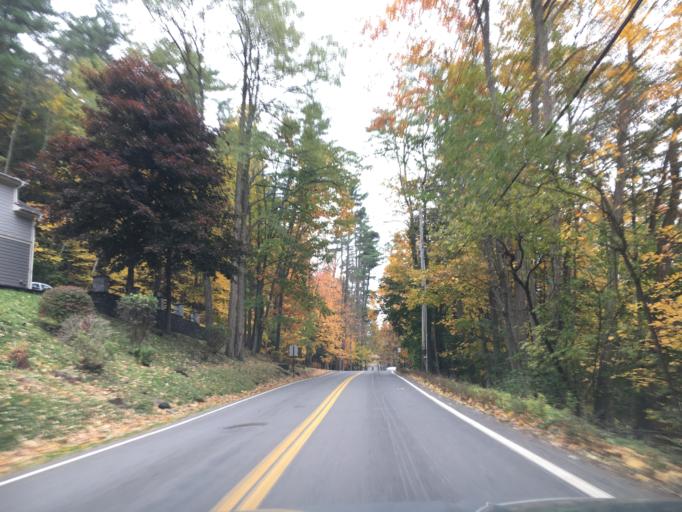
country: US
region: New York
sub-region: Otsego County
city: Cooperstown
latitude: 42.7008
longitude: -74.9153
